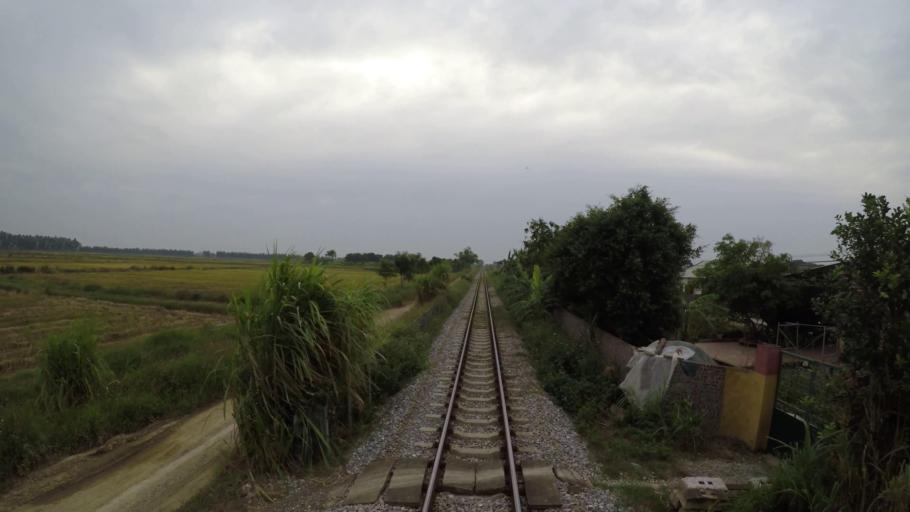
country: VN
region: Bac Ninh
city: Thua
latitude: 20.9643
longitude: 106.1768
